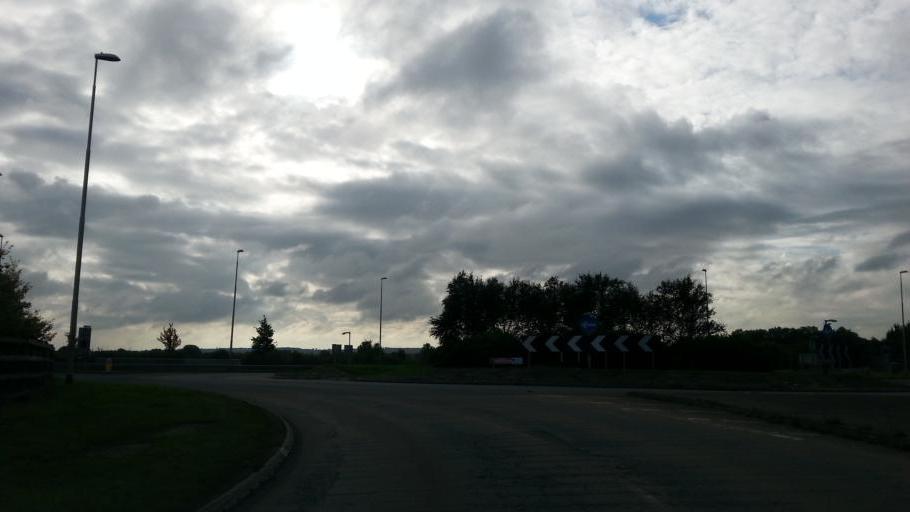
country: GB
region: England
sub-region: Bedford
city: Elstow
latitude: 52.1033
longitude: -0.4699
